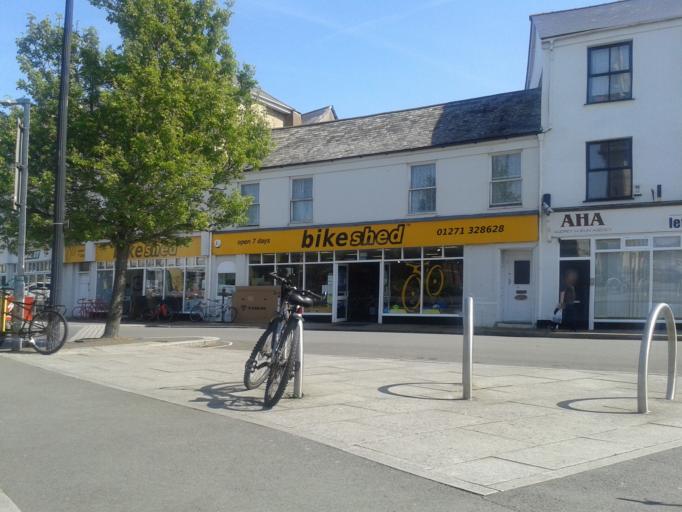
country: GB
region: England
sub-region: Devon
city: Barnstaple
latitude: 51.0777
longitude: -4.0582
